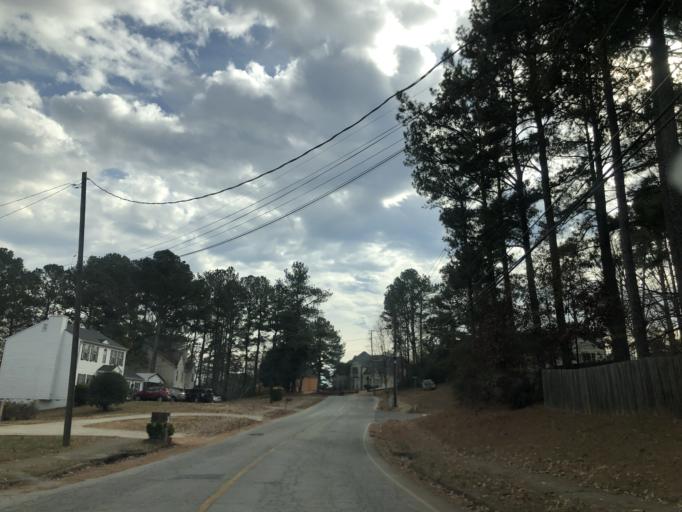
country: US
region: Georgia
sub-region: DeKalb County
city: Panthersville
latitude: 33.6717
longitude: -84.2155
